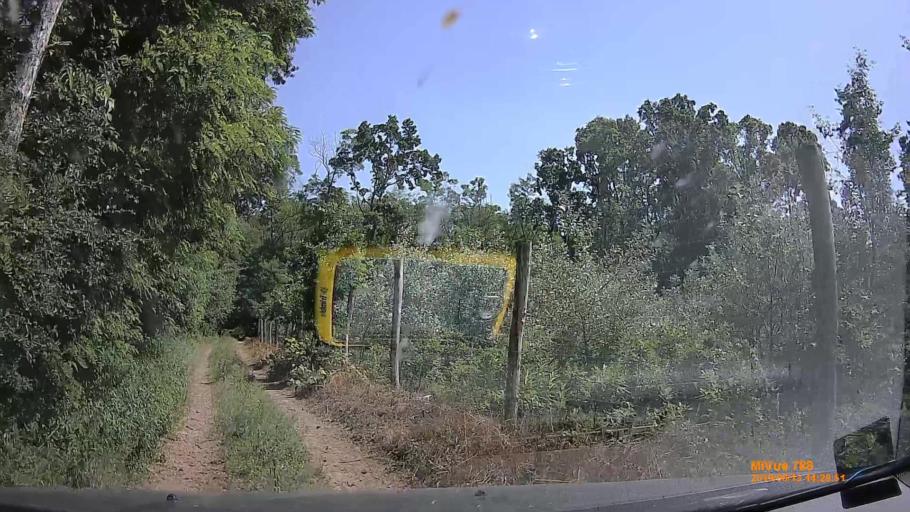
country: HU
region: Pest
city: Szada
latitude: 47.6041
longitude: 19.3032
